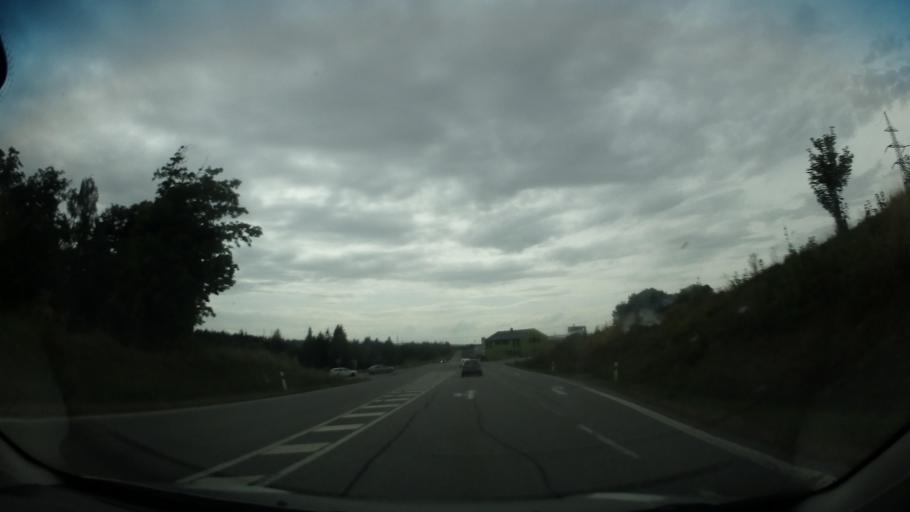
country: CZ
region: Vysocina
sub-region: Okres Zd'ar nad Sazavou
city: Zd'ar nad Sazavou
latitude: 49.5543
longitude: 15.9663
